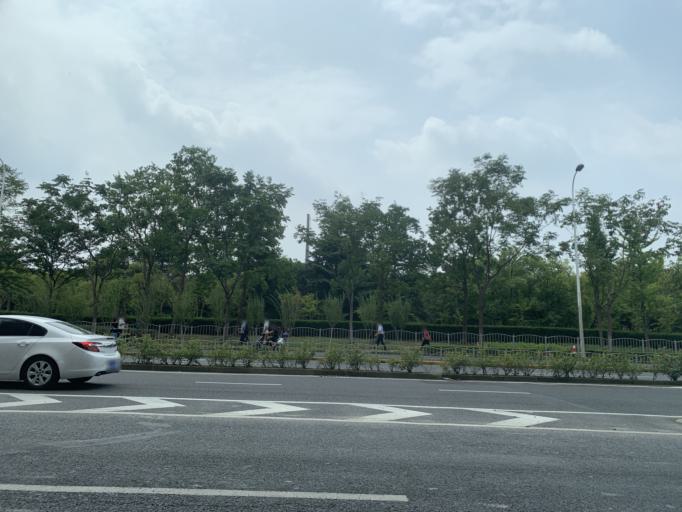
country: CN
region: Shanghai Shi
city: Huamu
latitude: 31.2057
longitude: 121.5573
